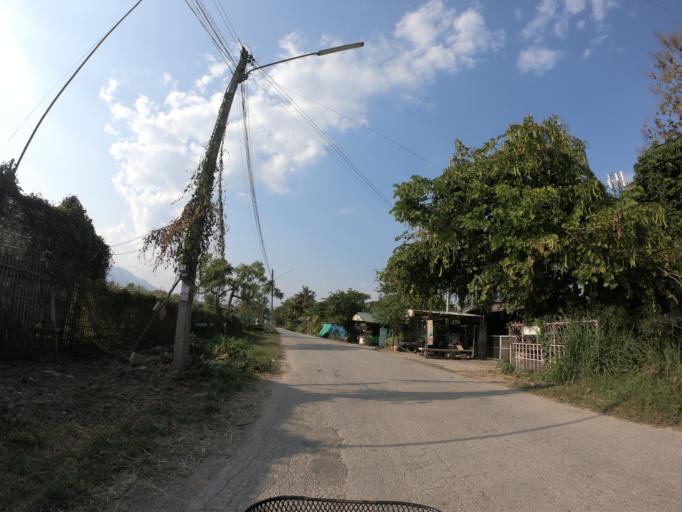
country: TH
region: Chiang Mai
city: Chiang Mai
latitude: 18.8324
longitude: 98.9904
